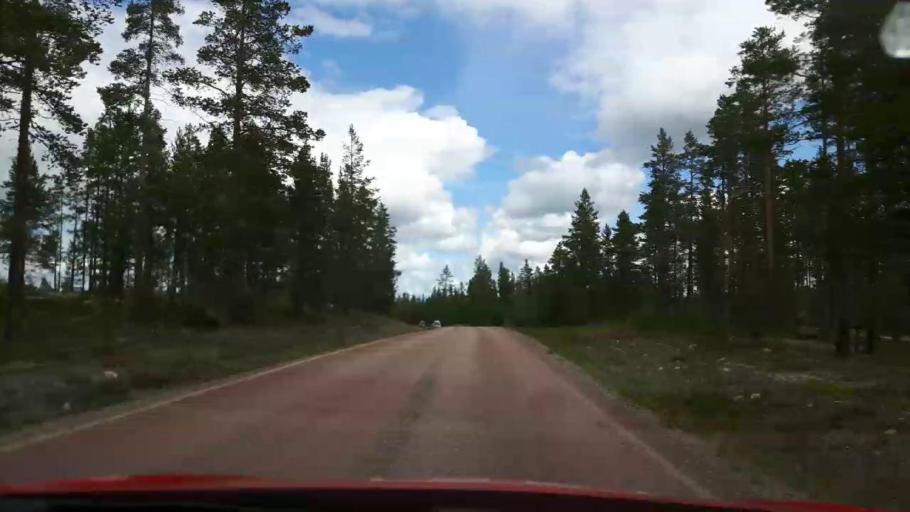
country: NO
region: Hedmark
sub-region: Trysil
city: Innbygda
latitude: 61.8905
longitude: 12.9844
